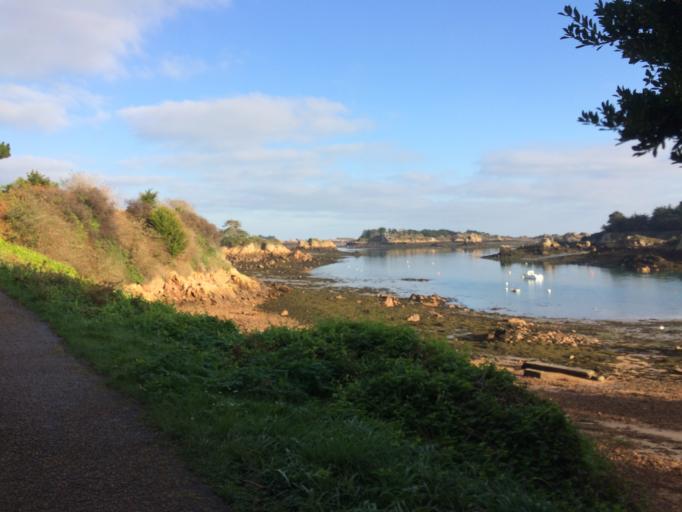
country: FR
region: Brittany
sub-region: Departement des Cotes-d'Armor
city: Ploubazlanec
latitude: 48.8390
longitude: -2.9974
